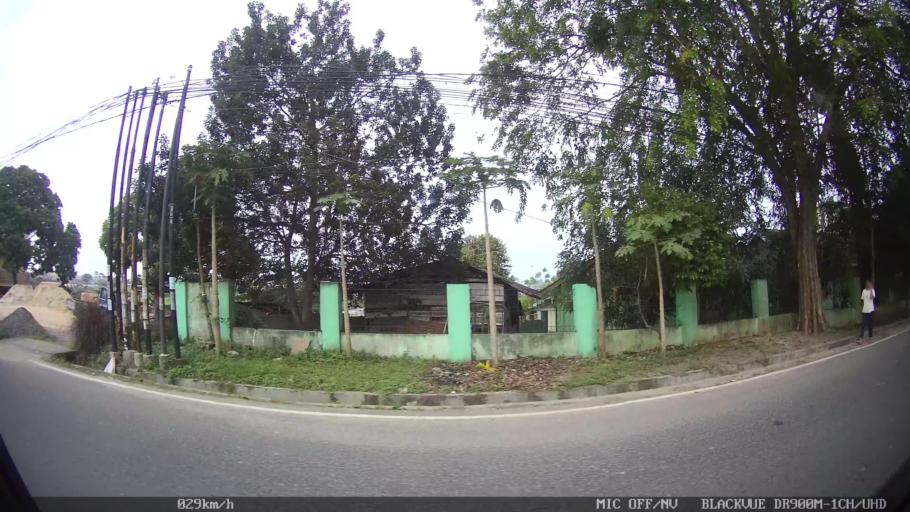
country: ID
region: Lampung
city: Kedaton
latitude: -5.4006
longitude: 105.2826
